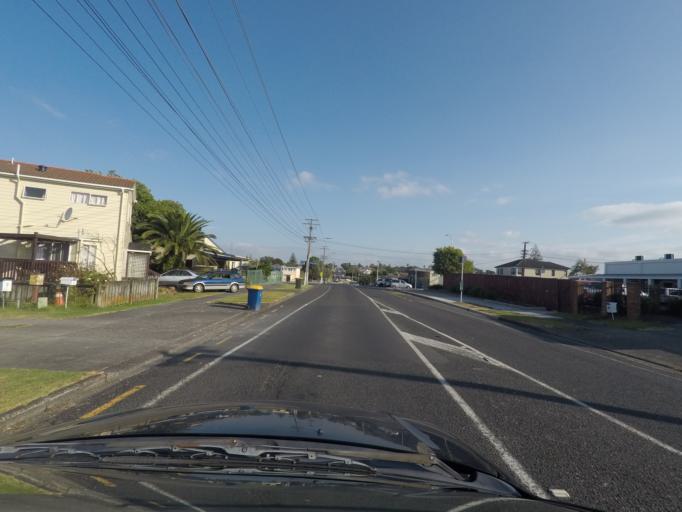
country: NZ
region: Auckland
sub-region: Auckland
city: Rosebank
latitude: -36.8592
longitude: 174.6439
